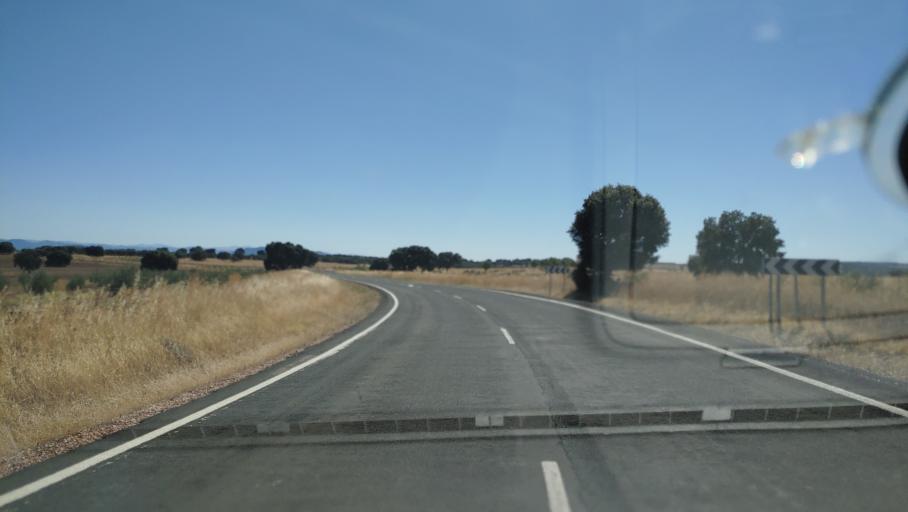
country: ES
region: Castille-La Mancha
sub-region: Provincia de Ciudad Real
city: Albaladejo
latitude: 38.5450
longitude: -2.7872
